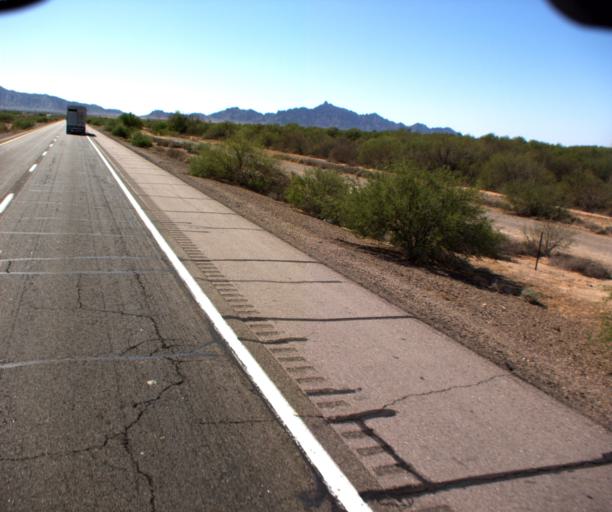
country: US
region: Arizona
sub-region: Yuma County
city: Wellton
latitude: 32.7541
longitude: -113.6537
